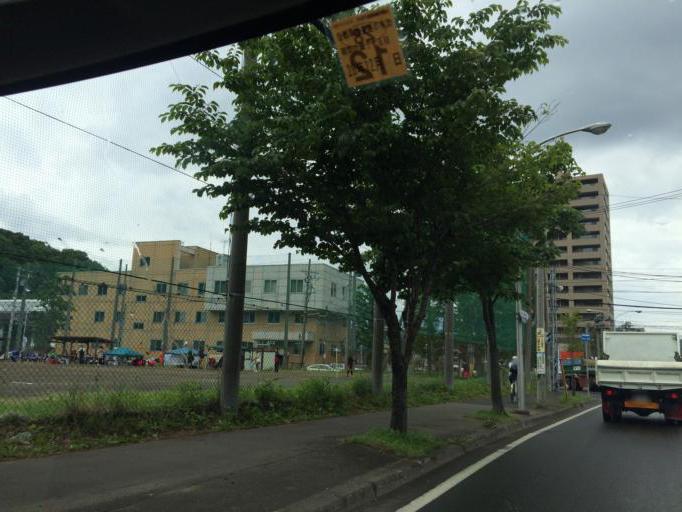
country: JP
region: Hokkaido
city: Sapporo
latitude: 43.0297
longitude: 141.3378
